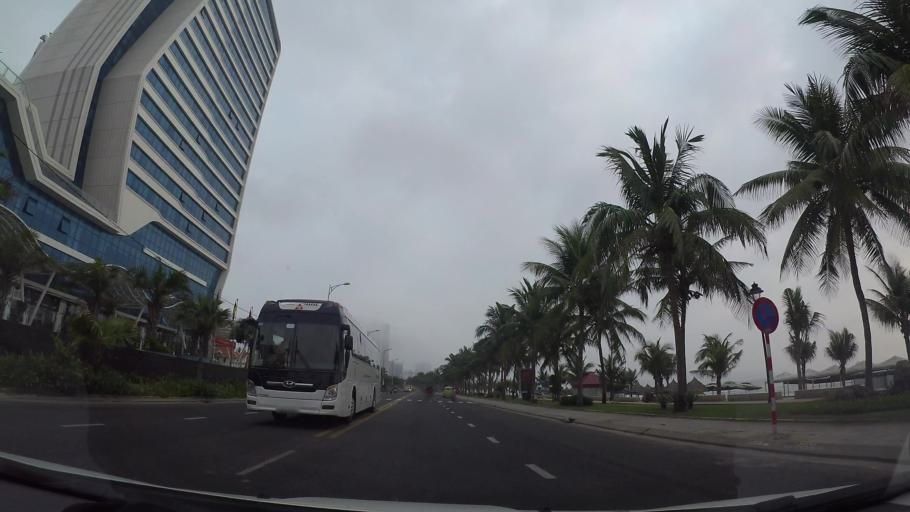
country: VN
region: Da Nang
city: Son Tra
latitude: 16.0615
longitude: 108.2464
